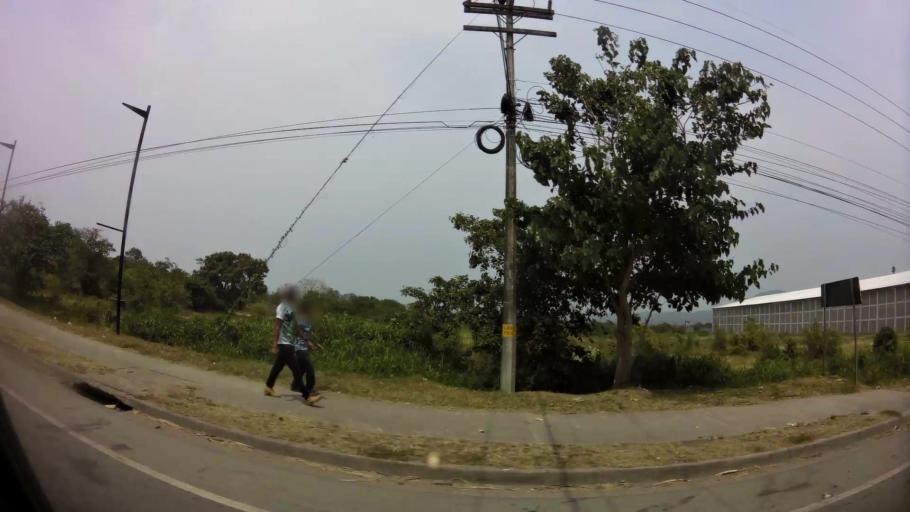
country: HN
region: Cortes
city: Villanueva
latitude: 15.3137
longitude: -87.9898
